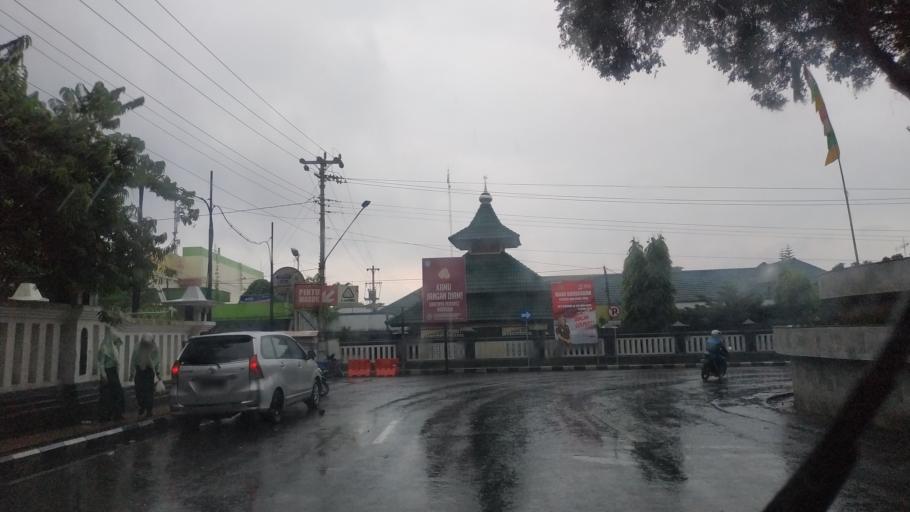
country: ID
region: Central Java
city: Magelang
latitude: -7.3158
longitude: 110.1759
